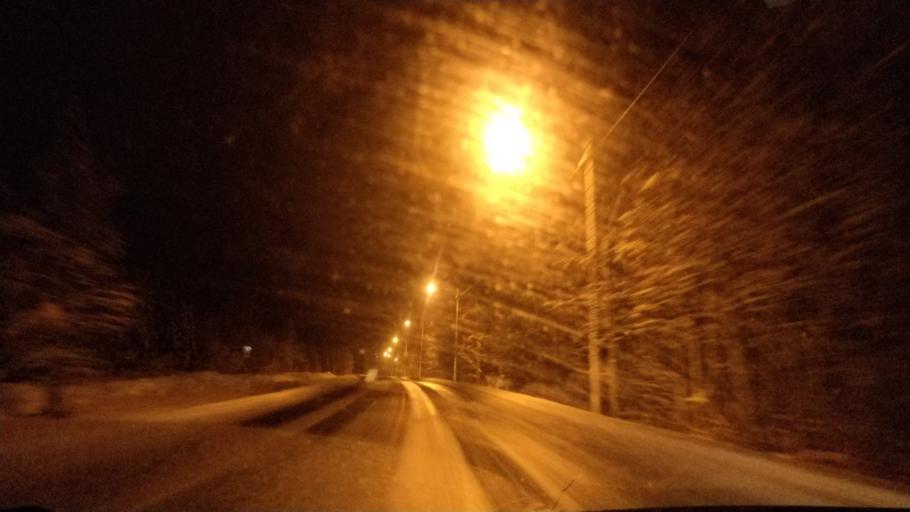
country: FI
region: Lapland
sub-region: Rovaniemi
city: Rovaniemi
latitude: 66.4019
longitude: 25.3893
